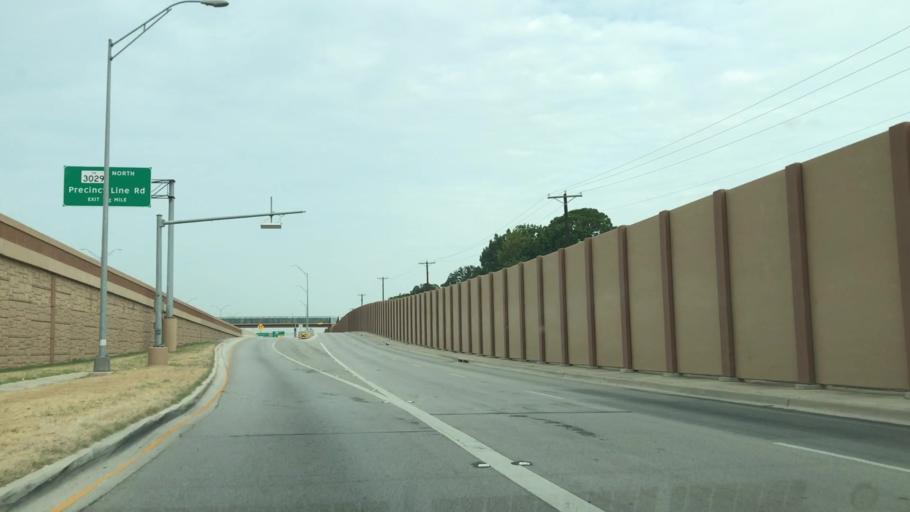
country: US
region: Texas
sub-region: Tarrant County
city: Hurst
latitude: 32.8401
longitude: -97.1686
